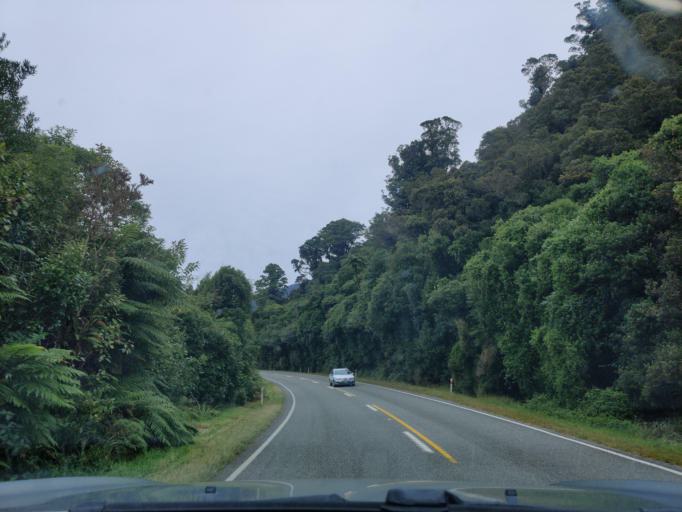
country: NZ
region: West Coast
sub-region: Buller District
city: Westport
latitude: -41.8325
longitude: 171.6570
